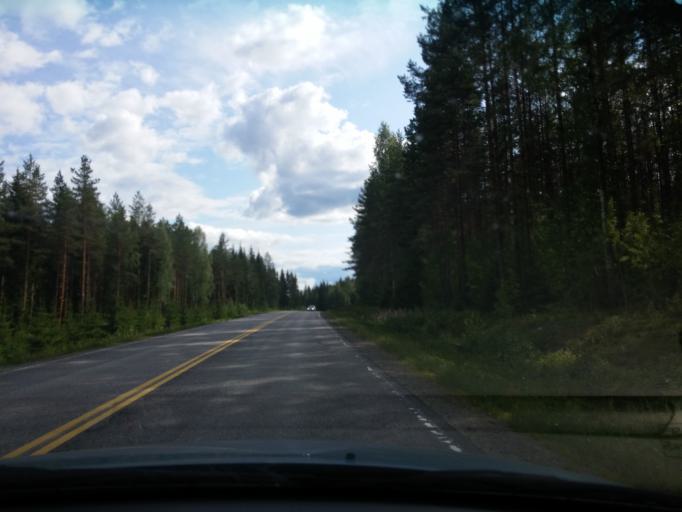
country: FI
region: Central Finland
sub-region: Keuruu
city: Keuruu
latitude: 62.3117
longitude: 24.7315
